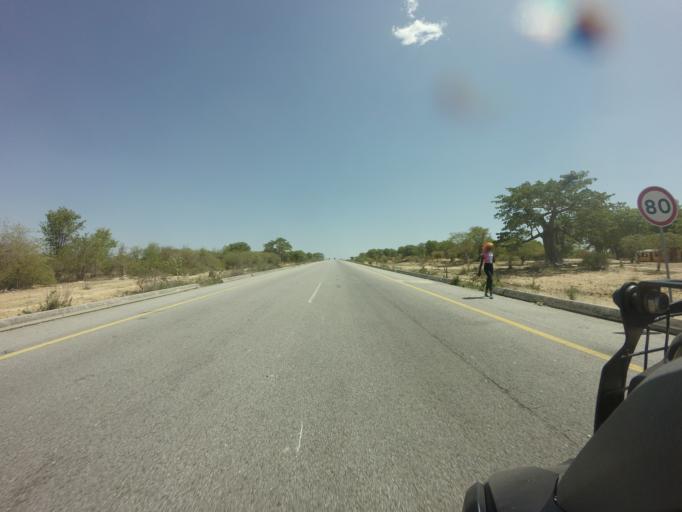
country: AO
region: Benguela
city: Benguela
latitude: -13.2205
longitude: 13.7669
